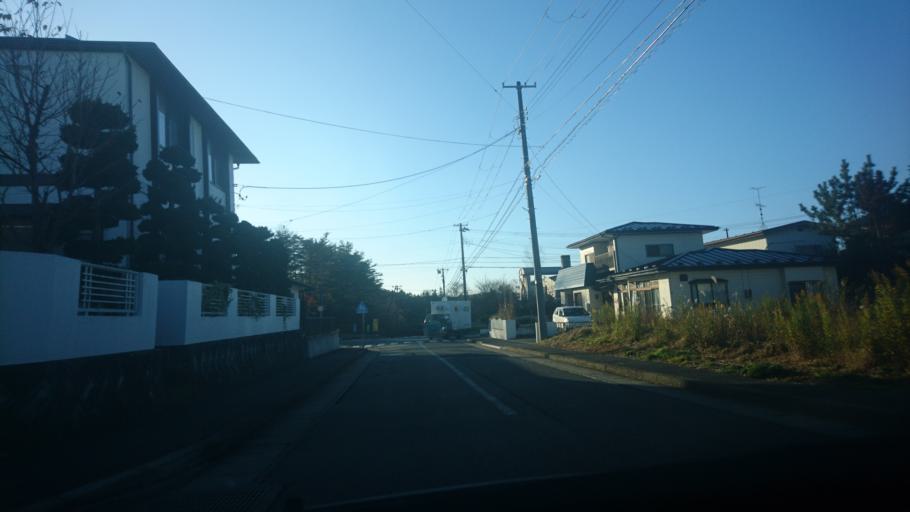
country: JP
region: Iwate
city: Ichinoseki
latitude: 38.9083
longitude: 141.1402
